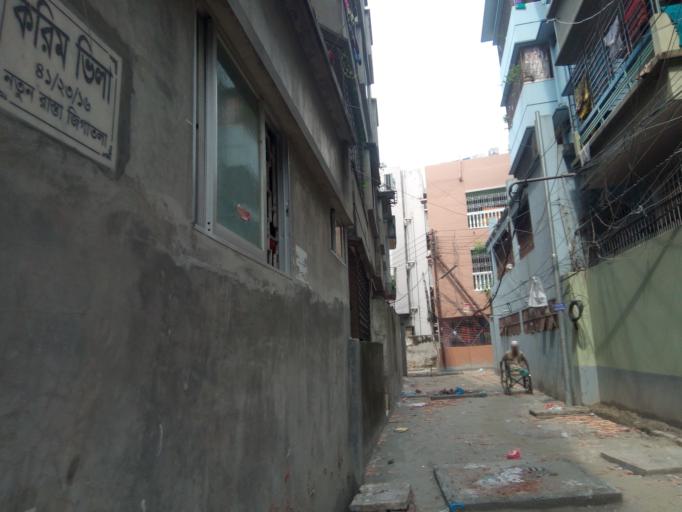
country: BD
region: Dhaka
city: Azimpur
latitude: 23.7419
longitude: 90.3706
